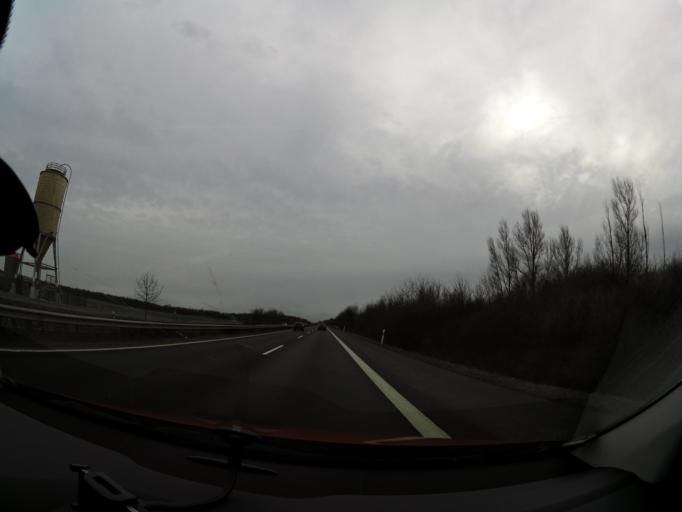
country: DE
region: Lower Saxony
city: Flothe
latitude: 52.0737
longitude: 10.4996
